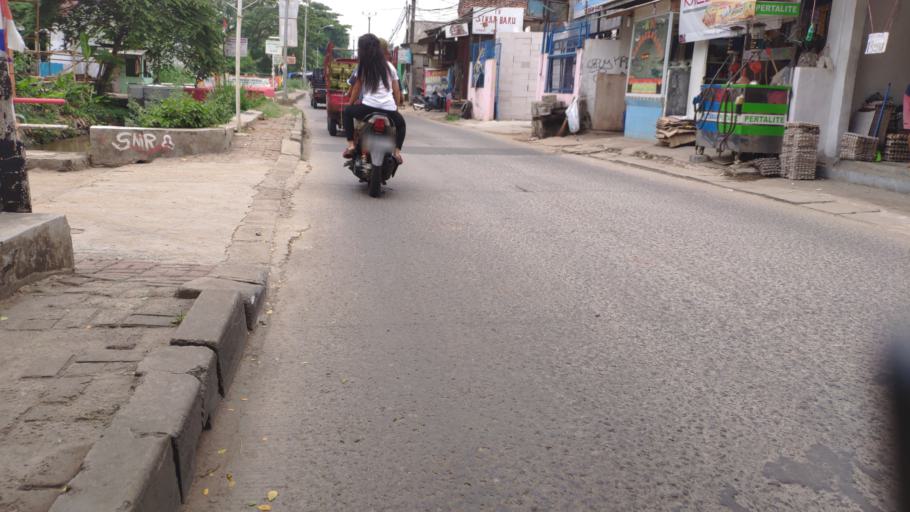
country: ID
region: West Java
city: Sawangan
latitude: -6.3852
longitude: 106.7911
